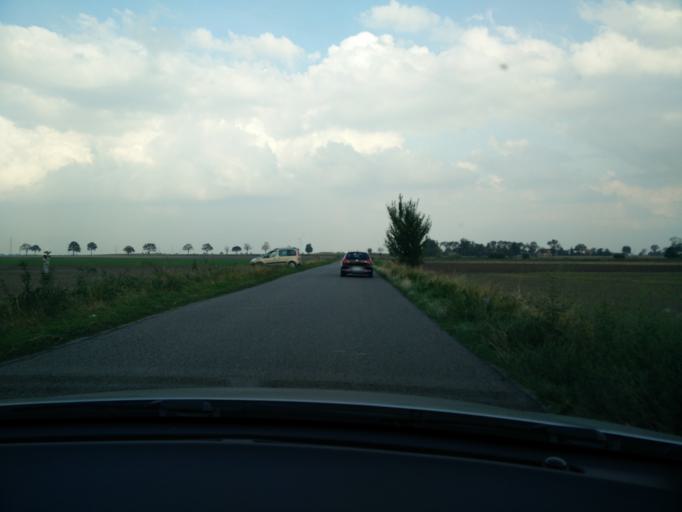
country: PL
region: Greater Poland Voivodeship
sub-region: Powiat wrzesinski
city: Wrzesnia
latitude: 52.2813
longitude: 17.5372
